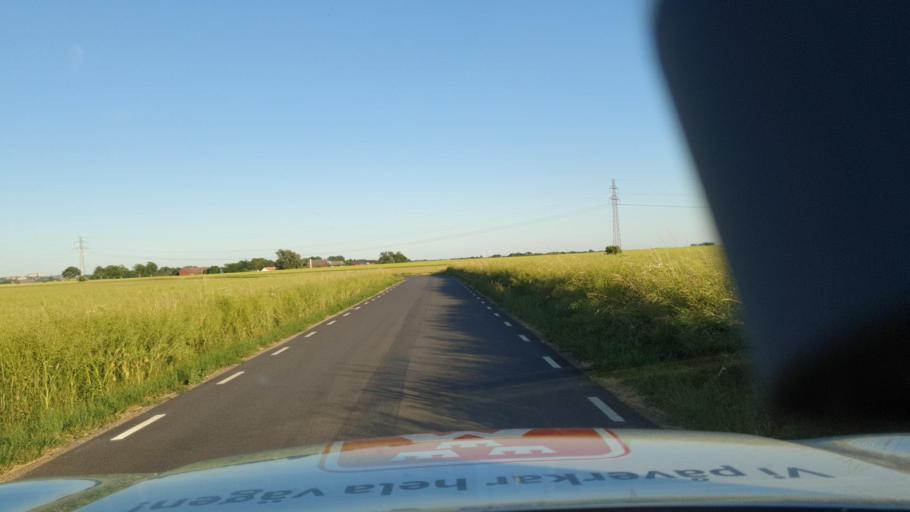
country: SE
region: Skane
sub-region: Kavlinge Kommun
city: Kaevlinge
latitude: 55.7461
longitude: 13.0899
